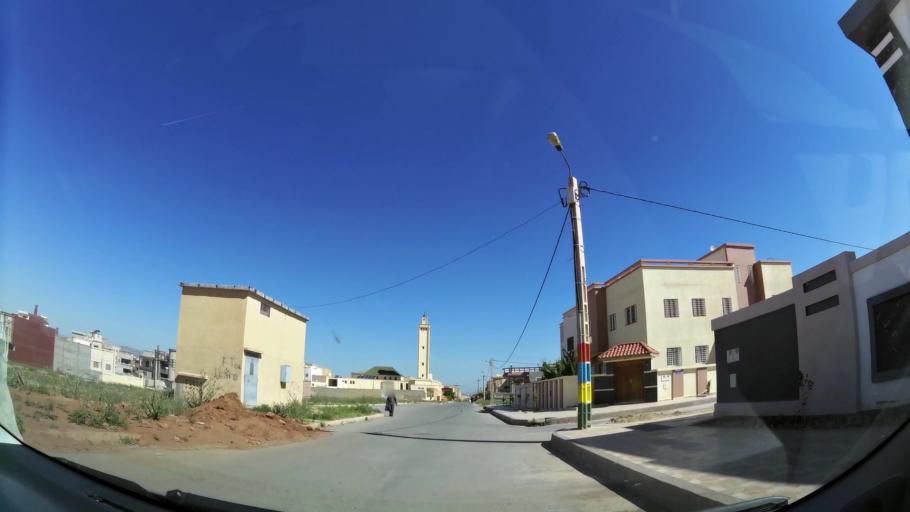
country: MA
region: Oriental
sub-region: Oujda-Angad
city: Oujda
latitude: 34.6536
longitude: -1.8863
